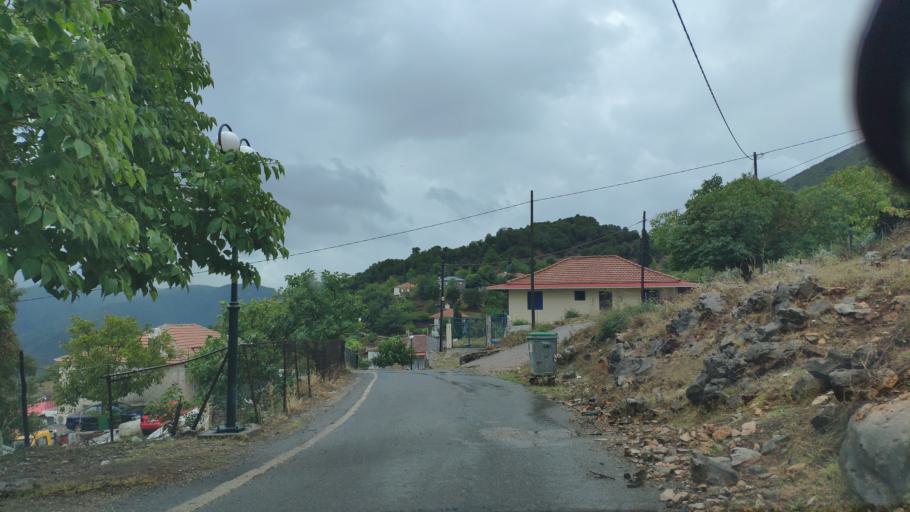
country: GR
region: Thessaly
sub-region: Nomos Kardhitsas
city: Anthiro
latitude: 39.1095
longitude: 21.4086
